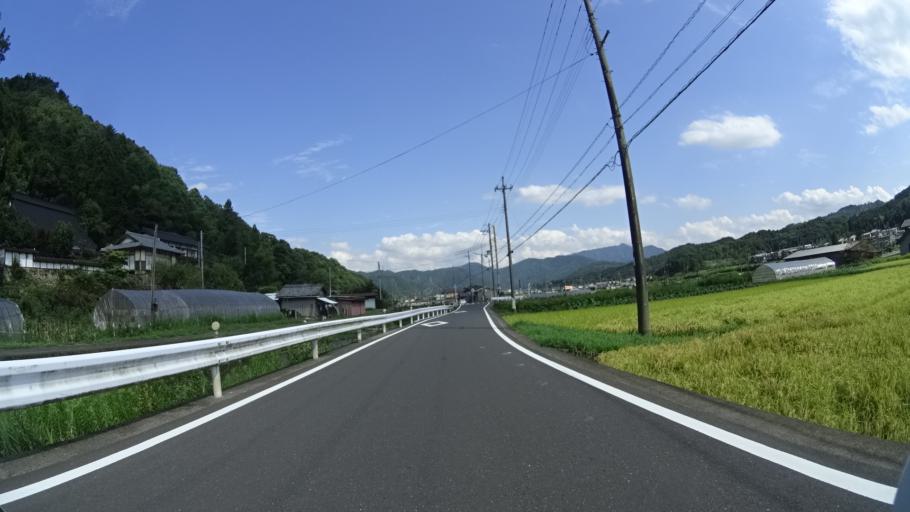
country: JP
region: Kyoto
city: Maizuru
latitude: 35.4316
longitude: 135.3134
